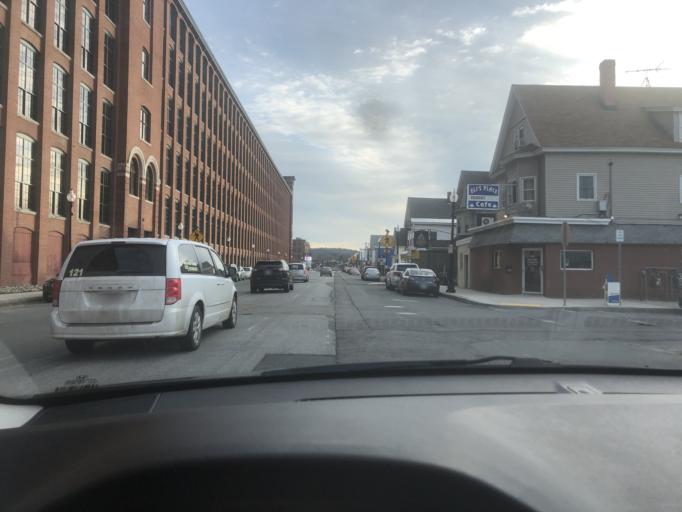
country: US
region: Massachusetts
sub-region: Essex County
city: Lawrence
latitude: 42.7028
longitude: -71.1501
